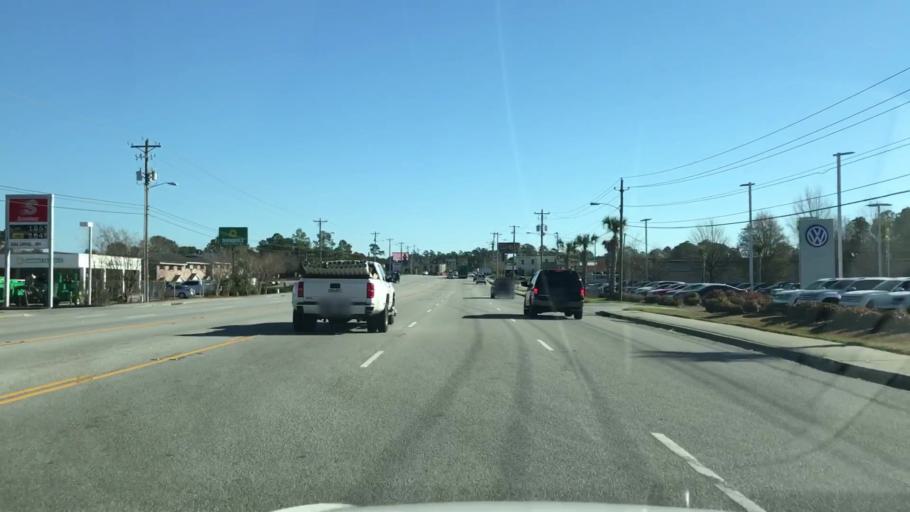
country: US
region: South Carolina
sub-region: Berkeley County
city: Hanahan
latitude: 32.9278
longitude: -80.0767
